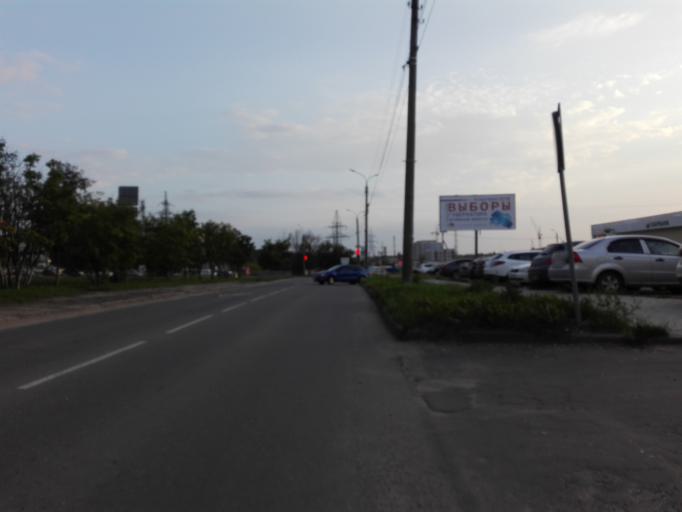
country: RU
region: Orjol
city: Orel
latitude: 53.0086
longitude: 36.1346
